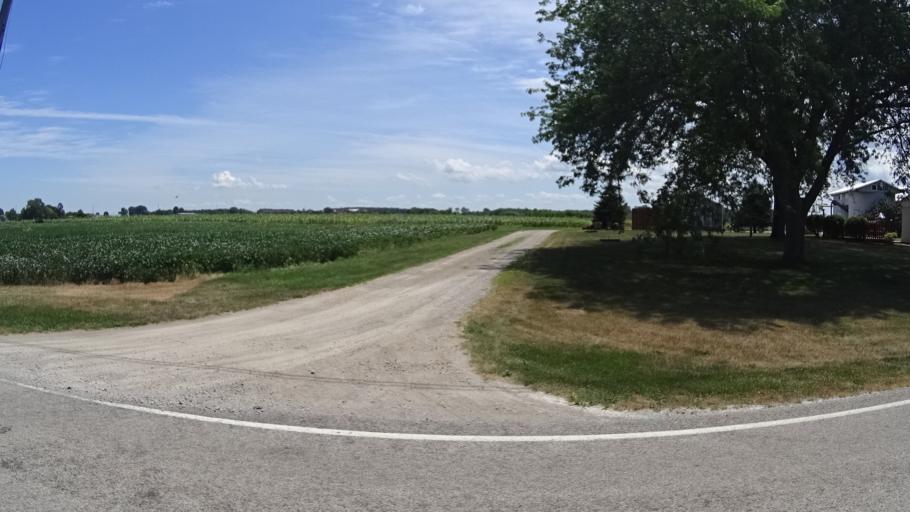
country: US
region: Ohio
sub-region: Erie County
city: Sandusky
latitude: 41.3913
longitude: -82.6591
